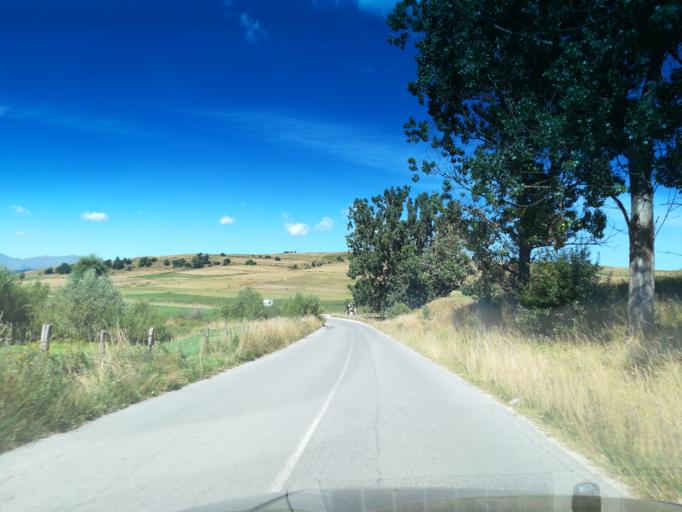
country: BG
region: Sofiya
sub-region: Obshtina Koprivshtitsa
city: Koprivshtitsa
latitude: 42.6027
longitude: 24.3805
